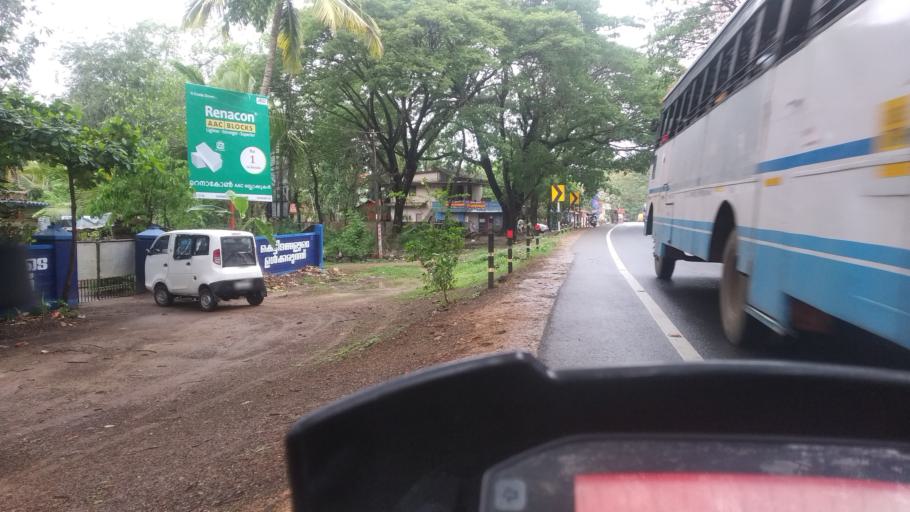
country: IN
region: Kerala
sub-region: Alappuzha
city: Alleppey
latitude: 9.3754
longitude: 76.3586
